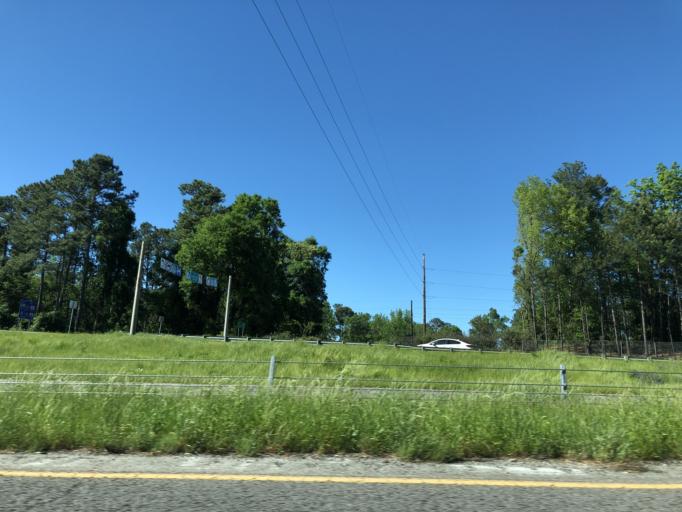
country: US
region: Georgia
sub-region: Clarke County
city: Country Club Estates
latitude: 33.9719
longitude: -83.4110
